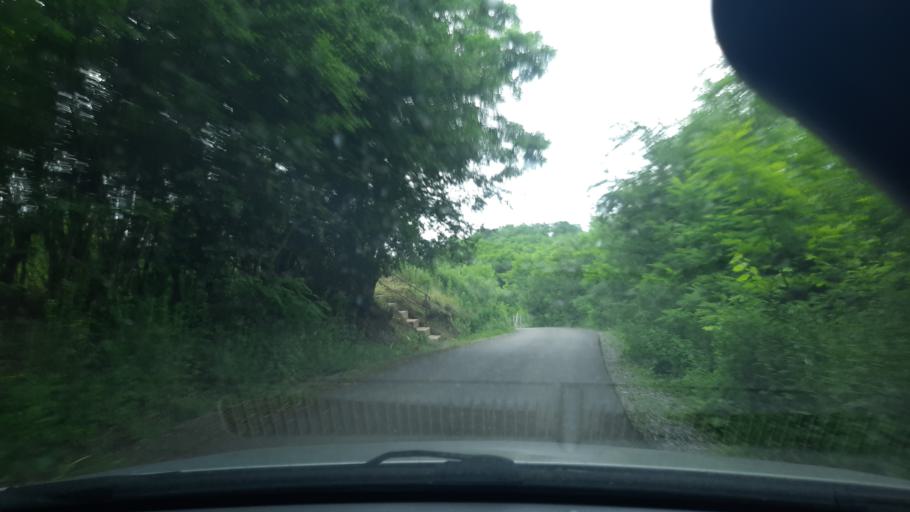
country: RS
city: Jarebice
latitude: 44.4953
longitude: 19.4773
